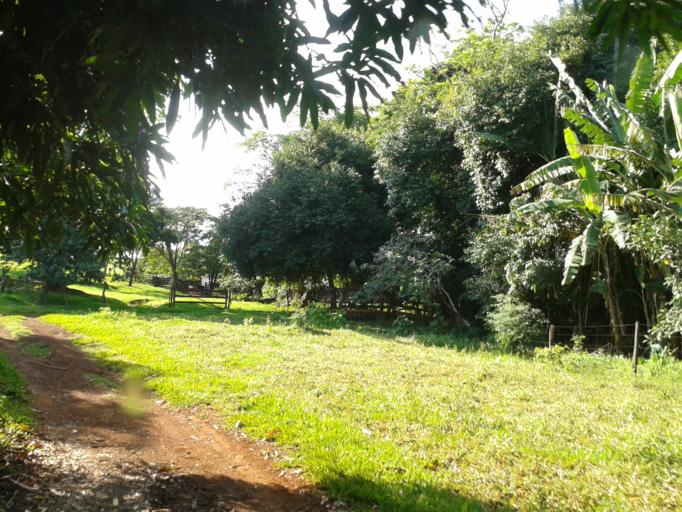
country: BR
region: Minas Gerais
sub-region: Centralina
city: Centralina
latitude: -18.7092
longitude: -49.1880
